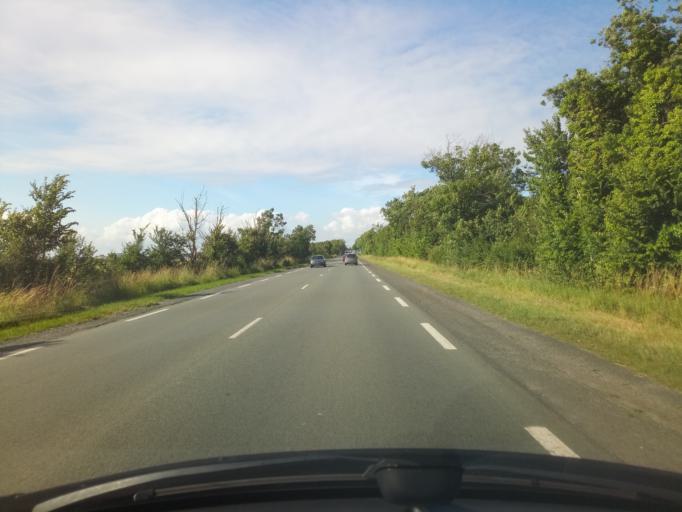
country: FR
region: Poitou-Charentes
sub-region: Departement de la Charente-Maritime
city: Marans
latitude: 46.2907
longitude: -0.9924
